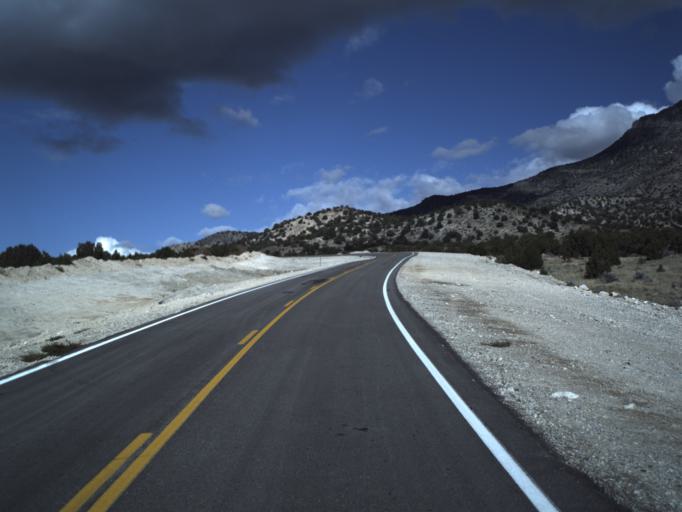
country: US
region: Utah
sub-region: Beaver County
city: Milford
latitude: 38.5109
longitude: -113.5238
